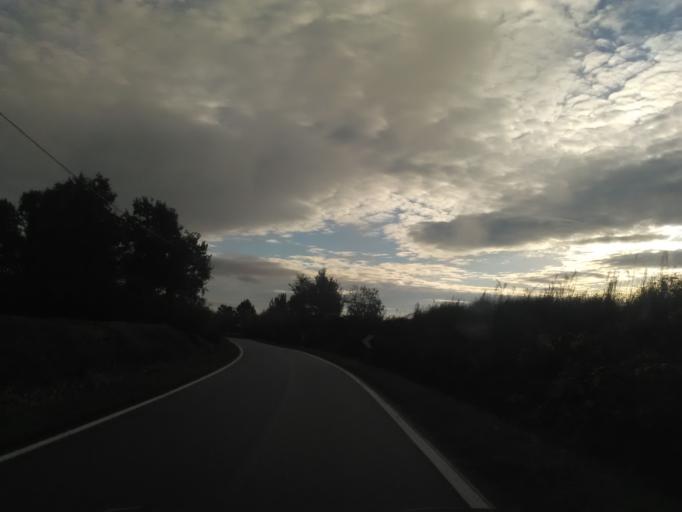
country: IT
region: Piedmont
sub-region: Provincia di Vercelli
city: Lenta
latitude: 45.5547
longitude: 8.3630
